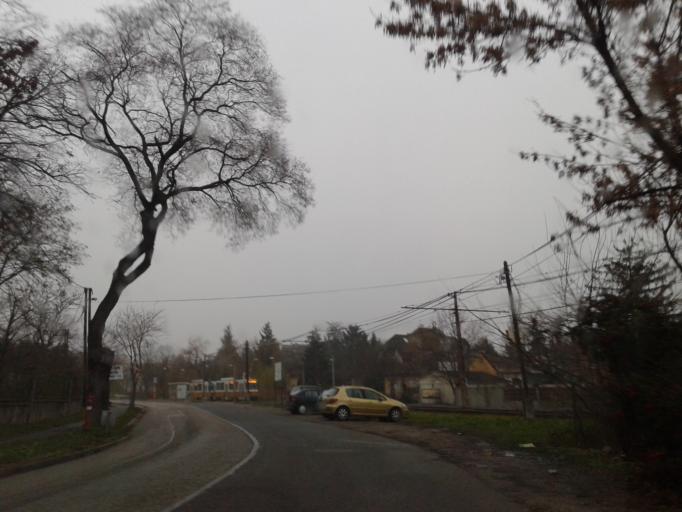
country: HU
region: Budapest
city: Budapest XXII. keruelet
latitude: 47.4376
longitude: 19.0315
